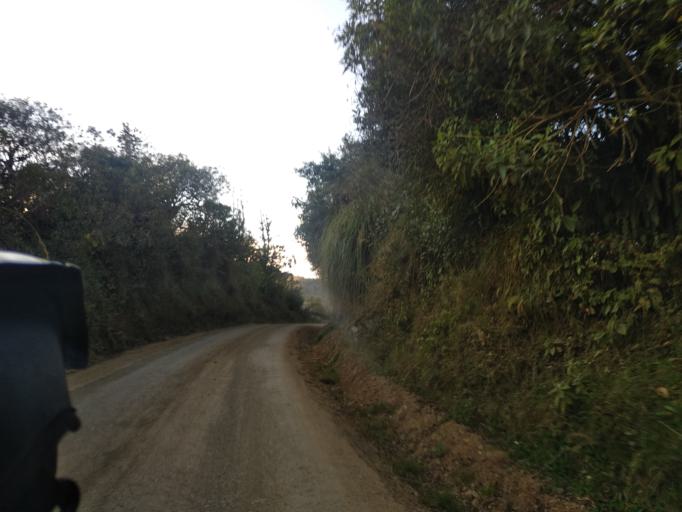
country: PE
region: Amazonas
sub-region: Provincia de Chachapoyas
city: Montevideo
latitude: -6.7188
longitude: -77.8663
